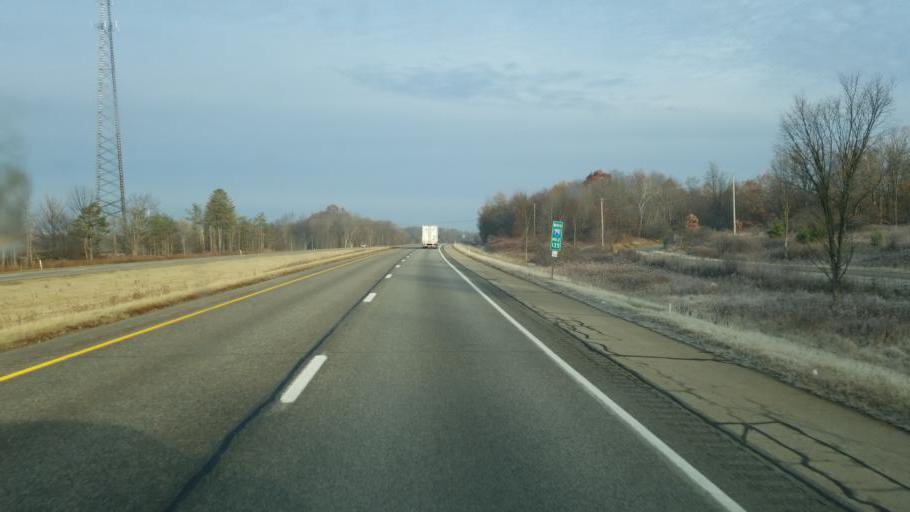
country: US
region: Pennsylvania
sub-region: Crawford County
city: Cochranton
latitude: 41.4606
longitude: -80.1650
